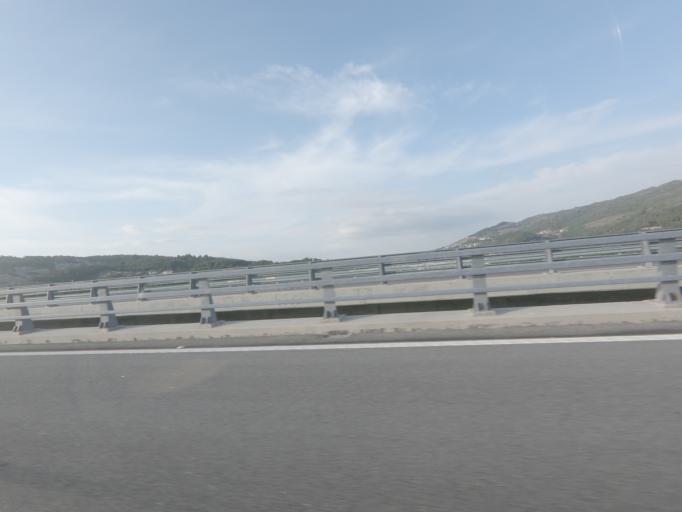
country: PT
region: Vila Real
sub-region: Vila Pouca de Aguiar
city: Vila Pouca de Aguiar
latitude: 41.4840
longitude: -7.6570
